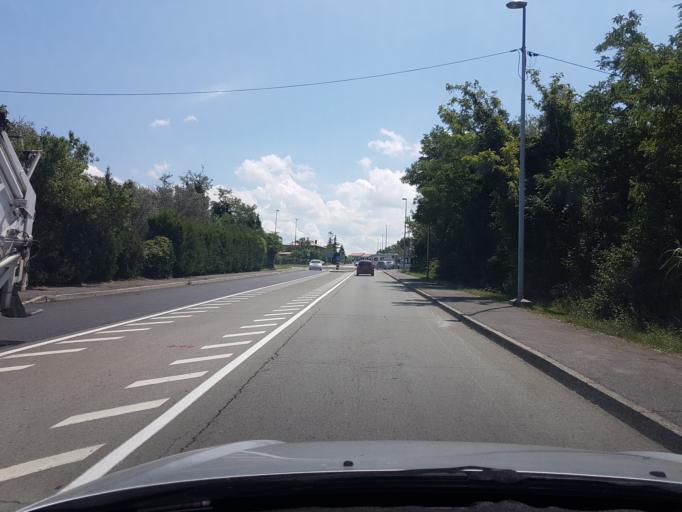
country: SI
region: Koper-Capodistria
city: Prade
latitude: 45.5449
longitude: 13.7652
